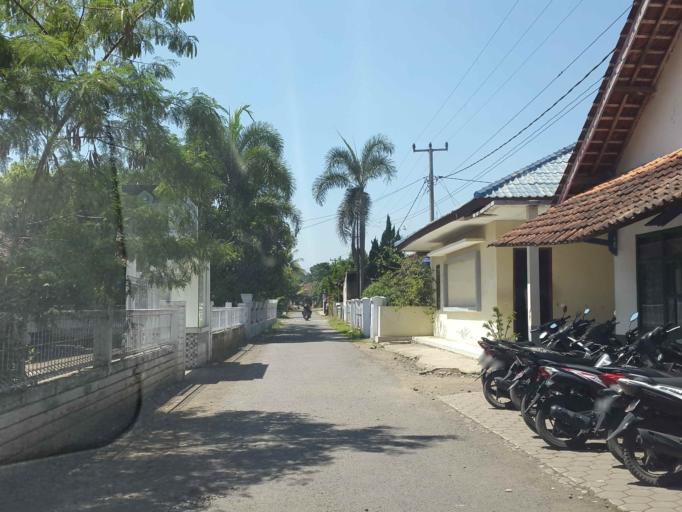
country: ID
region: West Java
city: Ciranjang-hilir
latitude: -6.7917
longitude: 107.2651
